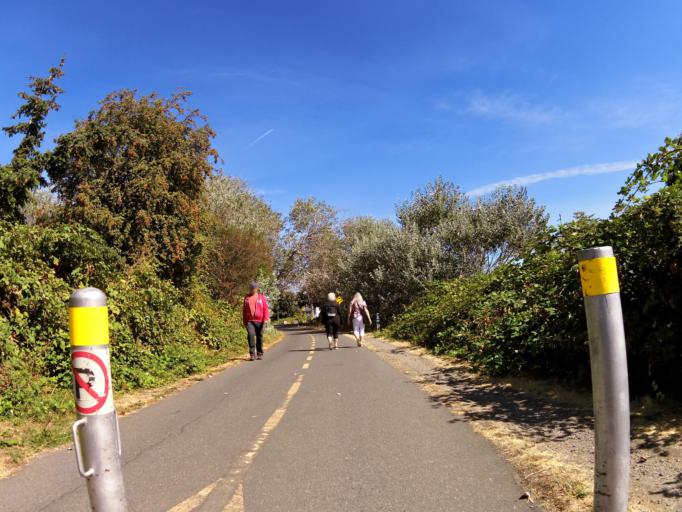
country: CA
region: British Columbia
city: Victoria
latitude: 48.4474
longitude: -123.3756
